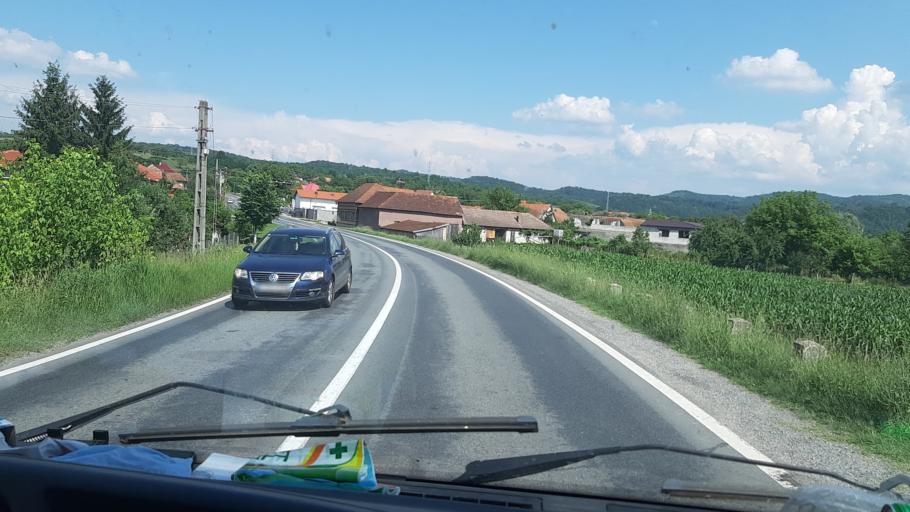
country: RO
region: Caras-Severin
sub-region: Comuna Ezeris
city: Ezeris
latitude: 45.3767
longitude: 21.9367
